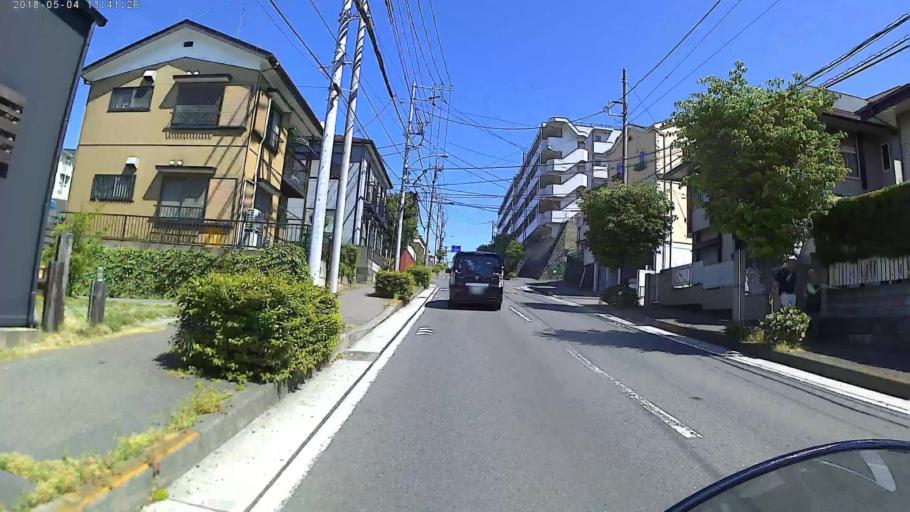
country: JP
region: Kanagawa
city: Minami-rinkan
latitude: 35.4376
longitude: 139.4601
